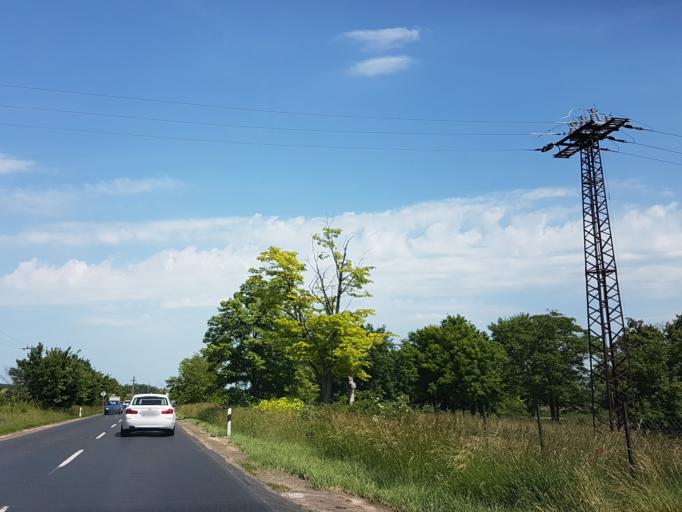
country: HU
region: Veszprem
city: Zanka
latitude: 46.8820
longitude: 17.7141
